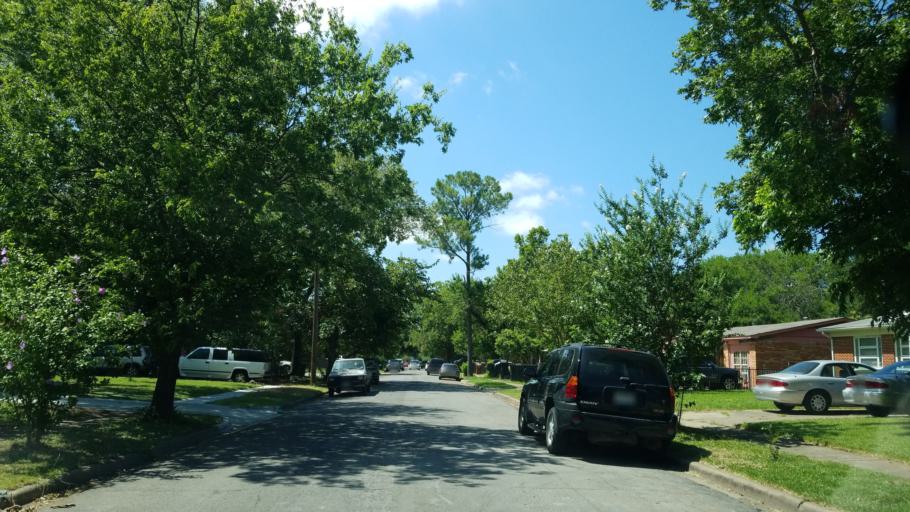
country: US
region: Texas
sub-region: Dallas County
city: Balch Springs
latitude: 32.7468
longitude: -96.6953
